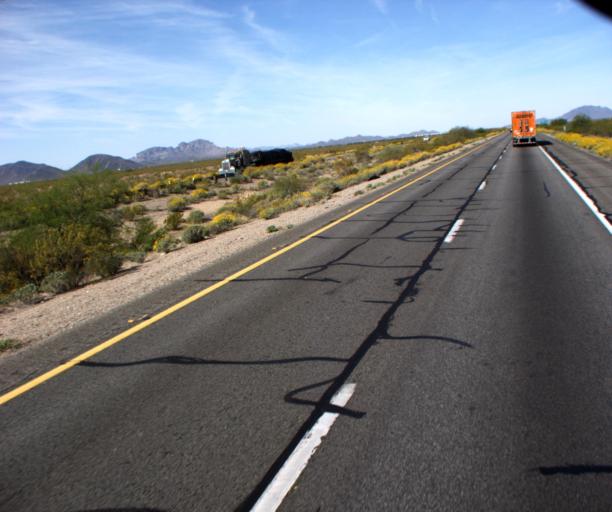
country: US
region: Arizona
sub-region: Maricopa County
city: Buckeye
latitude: 33.4791
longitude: -112.8544
